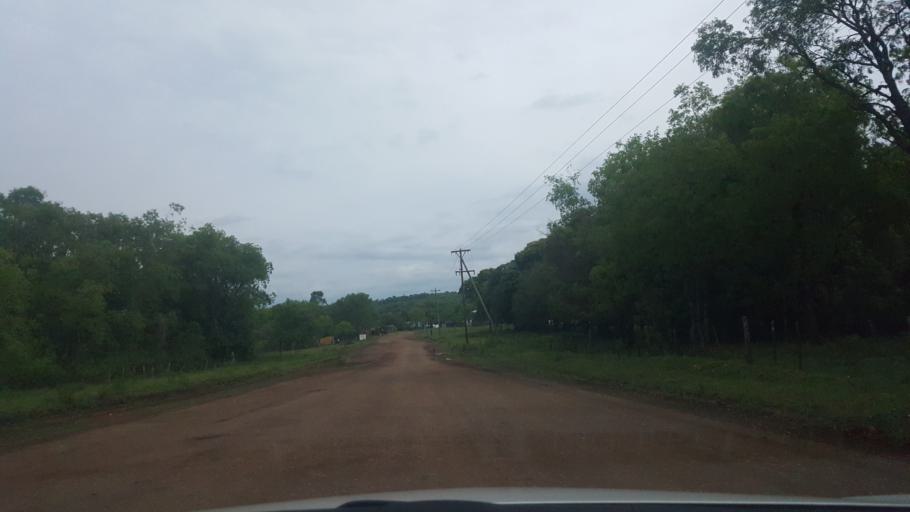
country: AR
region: Misiones
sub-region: Departamento de Candelaria
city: Candelaria
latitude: -27.5565
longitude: -55.7062
